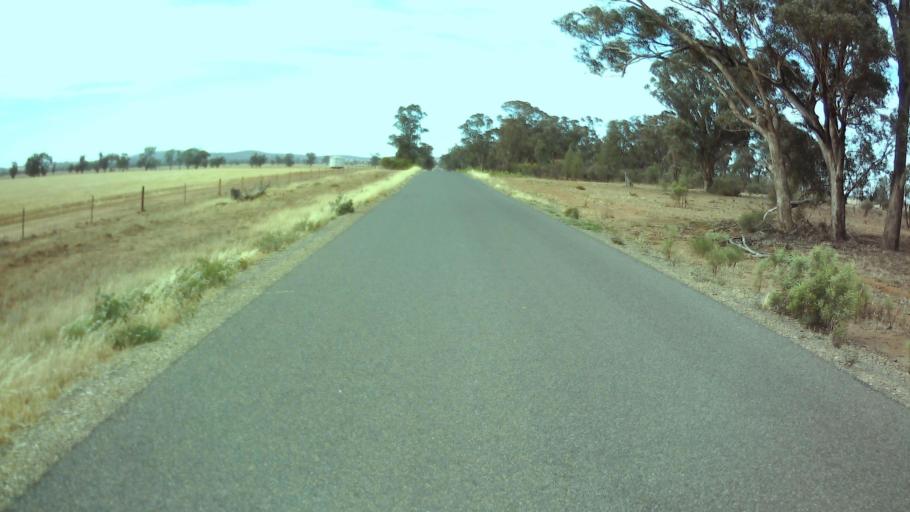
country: AU
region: New South Wales
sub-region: Weddin
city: Grenfell
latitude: -33.8863
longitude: 147.8551
